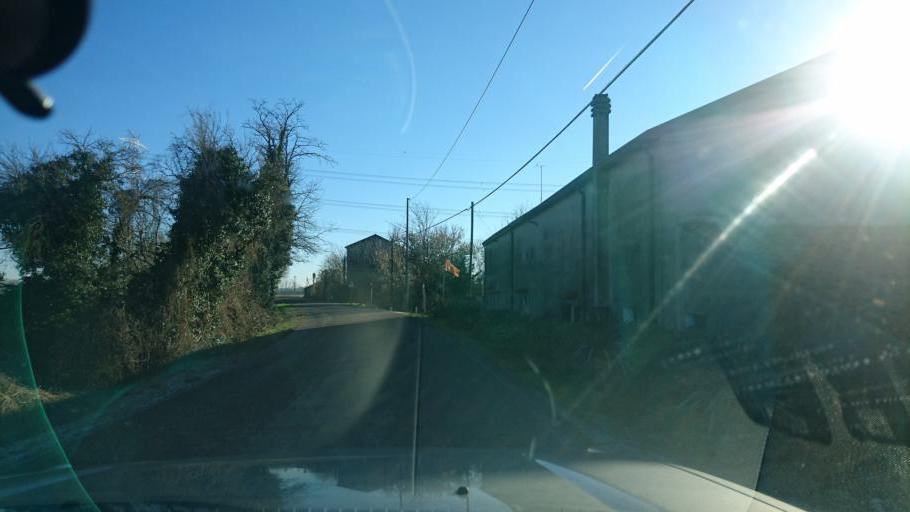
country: IT
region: Veneto
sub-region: Provincia di Venezia
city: Boscochiaro
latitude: 45.1167
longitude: 12.1275
